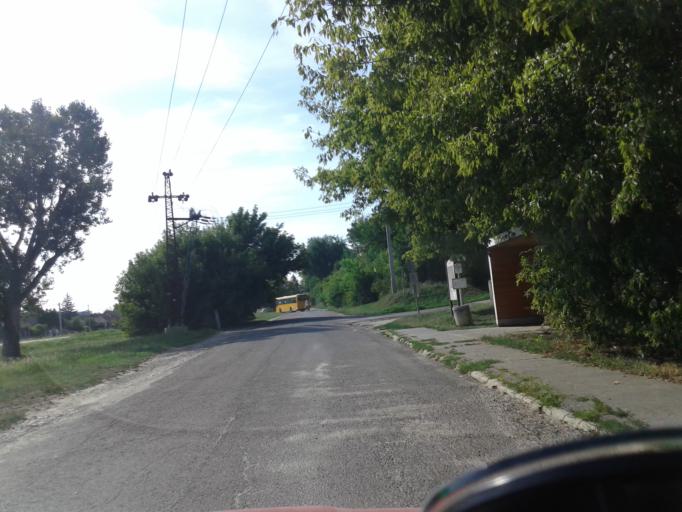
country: HU
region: Pest
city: Godollo
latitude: 47.5974
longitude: 19.3960
